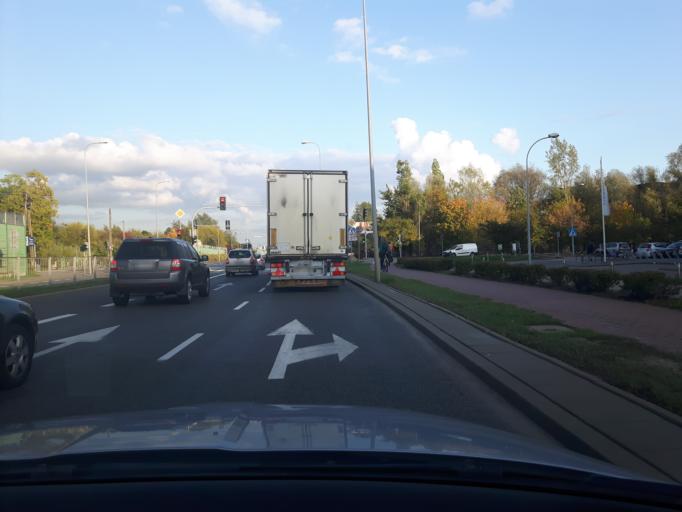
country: PL
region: Masovian Voivodeship
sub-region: Warszawa
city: Ursynow
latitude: 52.1548
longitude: 21.0061
